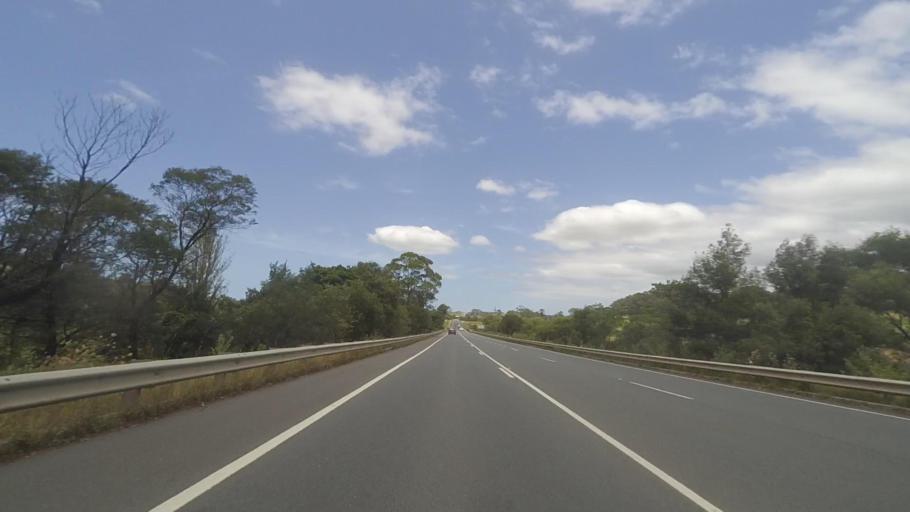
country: AU
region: New South Wales
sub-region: Shoalhaven Shire
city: Milton
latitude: -35.2668
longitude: 150.4247
